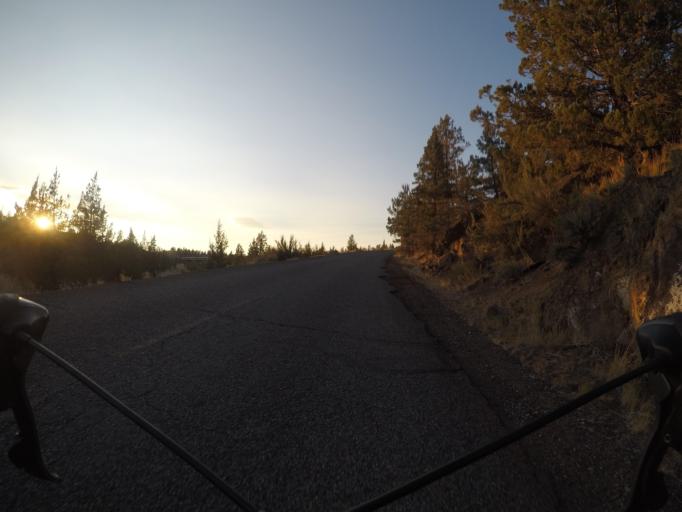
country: US
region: Oregon
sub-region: Deschutes County
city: Redmond
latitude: 44.2717
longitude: -121.2567
